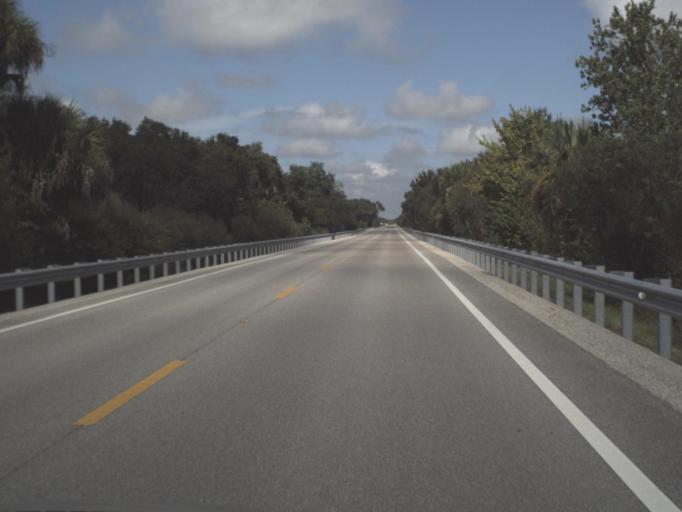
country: US
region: Florida
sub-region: Sarasota County
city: Lake Sarasota
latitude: 27.2262
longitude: -82.3016
